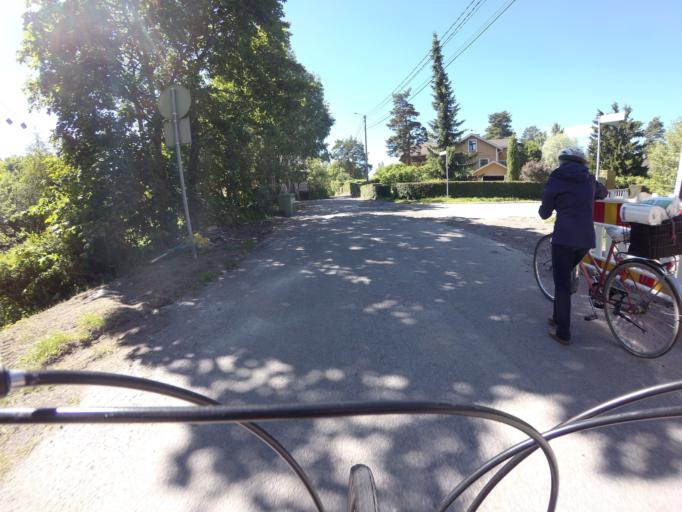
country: FI
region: Varsinais-Suomi
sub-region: Turku
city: Raisio
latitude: 60.4518
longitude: 22.2106
